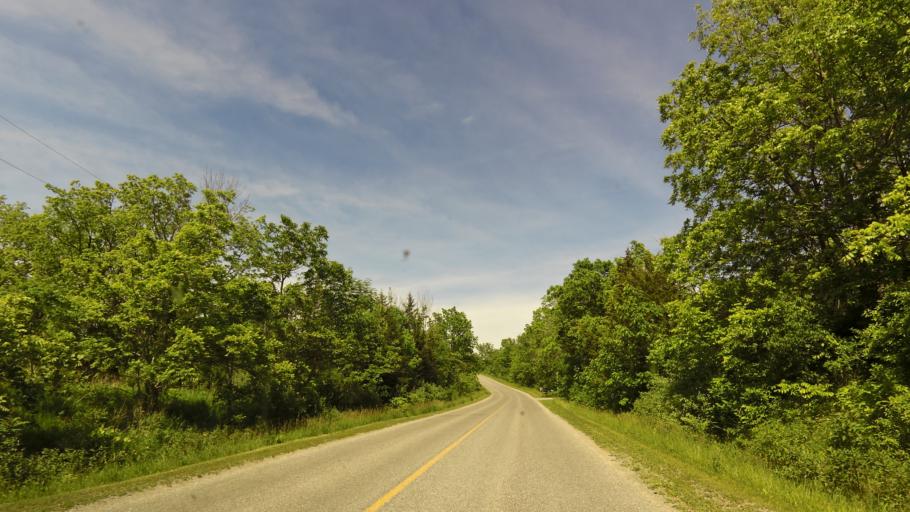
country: CA
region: Ontario
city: Norfolk County
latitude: 42.7309
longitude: -80.2891
